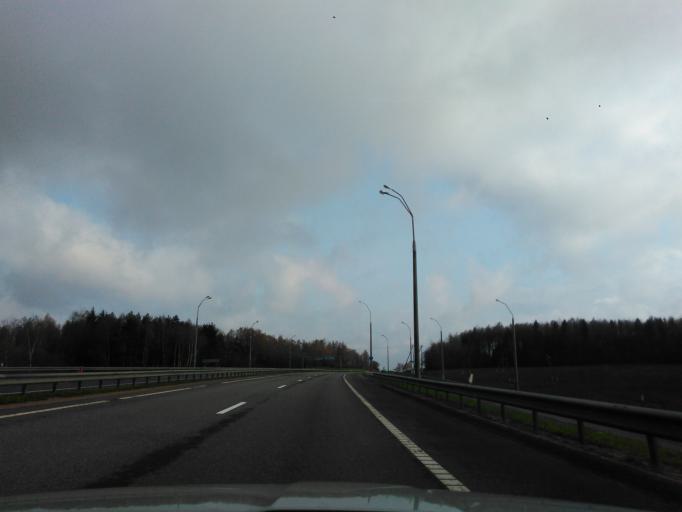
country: BY
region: Minsk
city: Lahoysk
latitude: 54.1750
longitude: 27.8194
